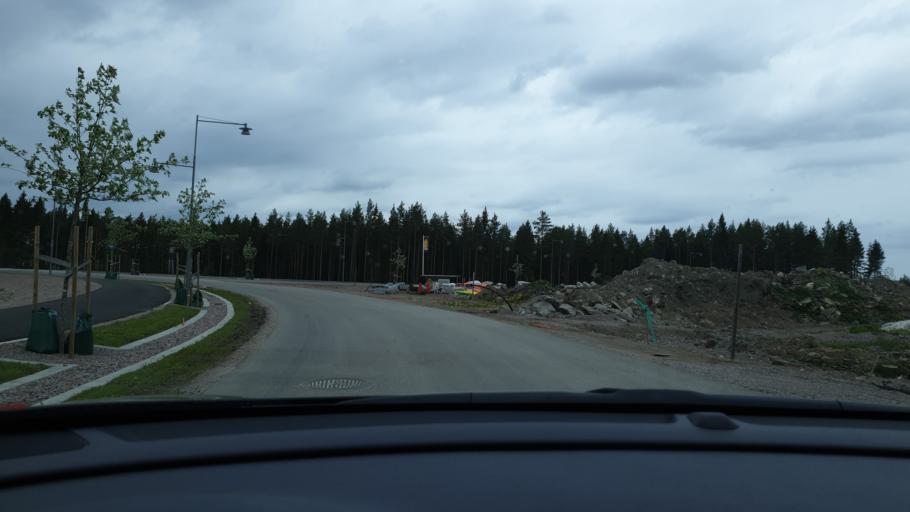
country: SE
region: Gaevleborg
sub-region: Gavle Kommun
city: Gavle
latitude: 60.6413
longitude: 17.1535
